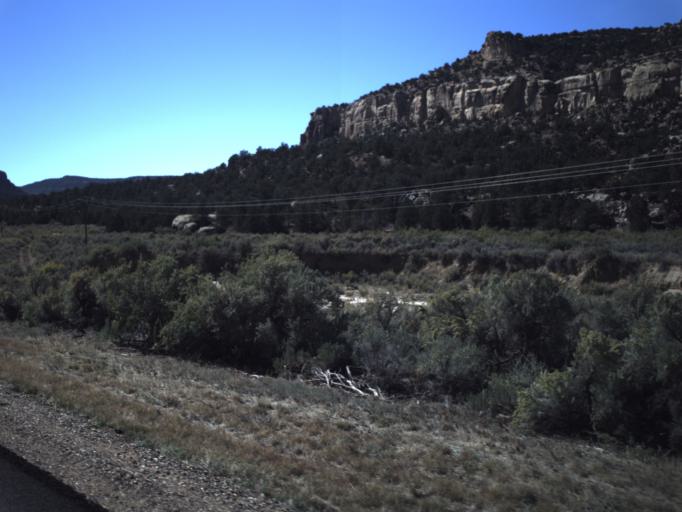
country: US
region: Utah
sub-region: Wayne County
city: Loa
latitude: 37.7476
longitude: -111.7048
